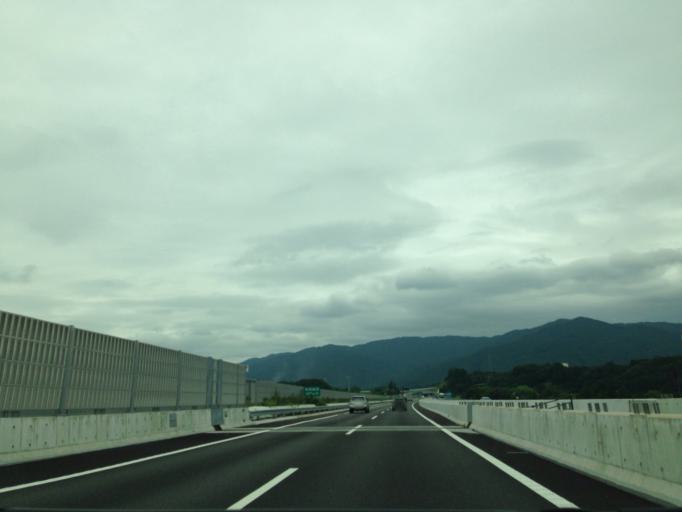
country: JP
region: Aichi
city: Shinshiro
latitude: 34.9205
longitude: 137.5574
